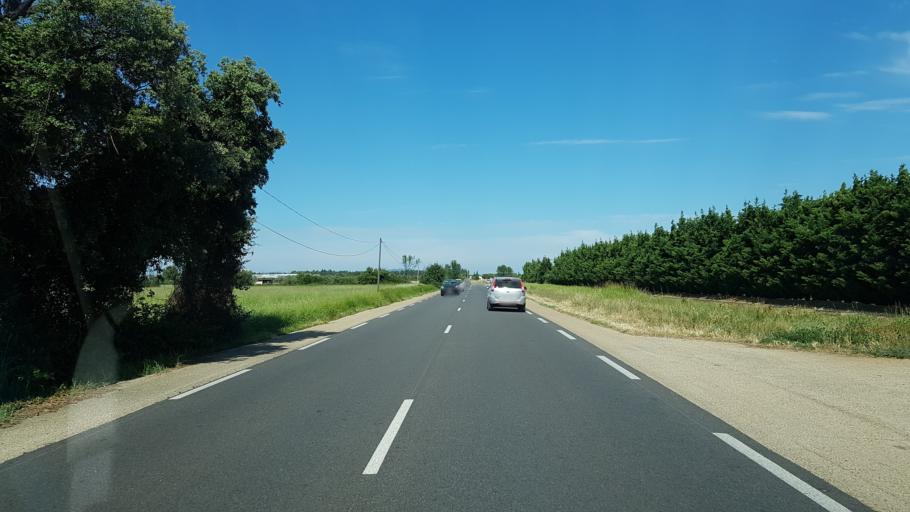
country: FR
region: Provence-Alpes-Cote d'Azur
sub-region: Departement des Bouches-du-Rhone
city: Paradou
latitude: 43.6691
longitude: 4.7455
